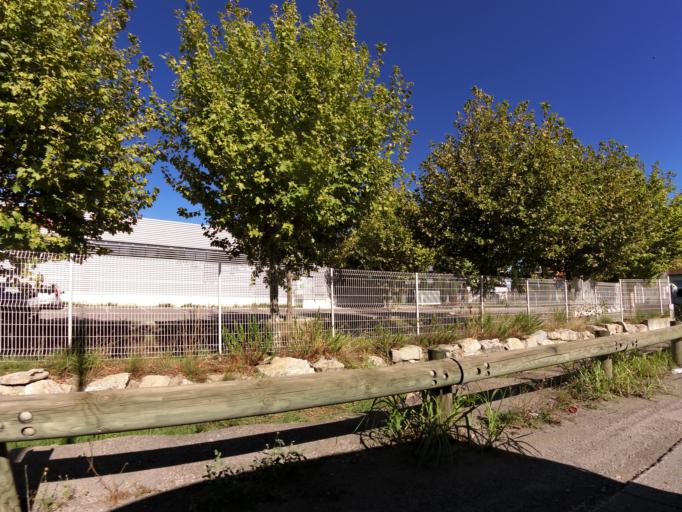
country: FR
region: Languedoc-Roussillon
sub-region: Departement du Gard
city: Caissargues
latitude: 43.8121
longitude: 4.3709
